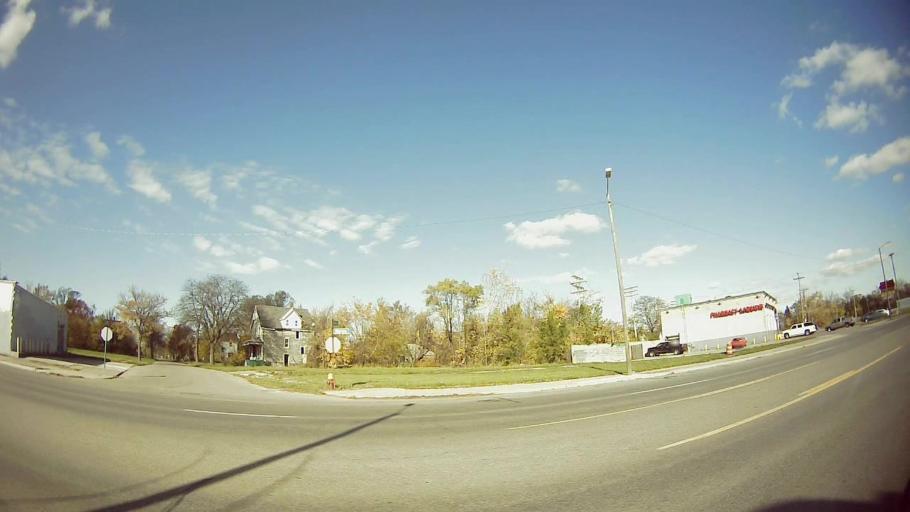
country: US
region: Michigan
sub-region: Wayne County
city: Dearborn
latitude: 42.3445
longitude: -83.1205
